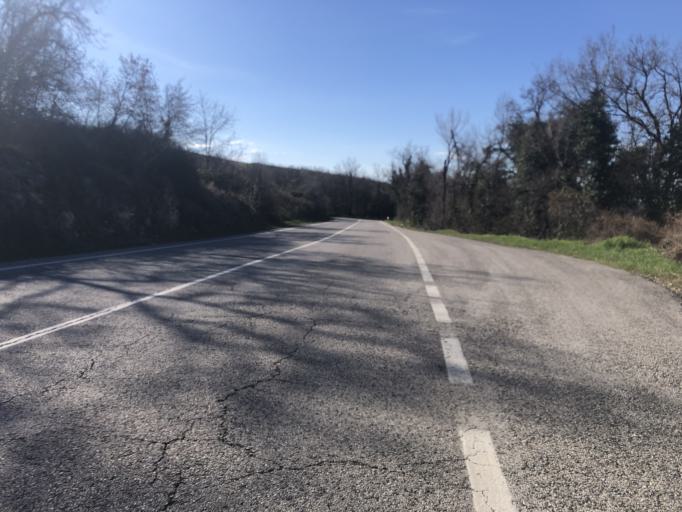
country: IT
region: Veneto
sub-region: Provincia di Verona
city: Volargne
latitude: 45.5411
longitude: 10.8338
